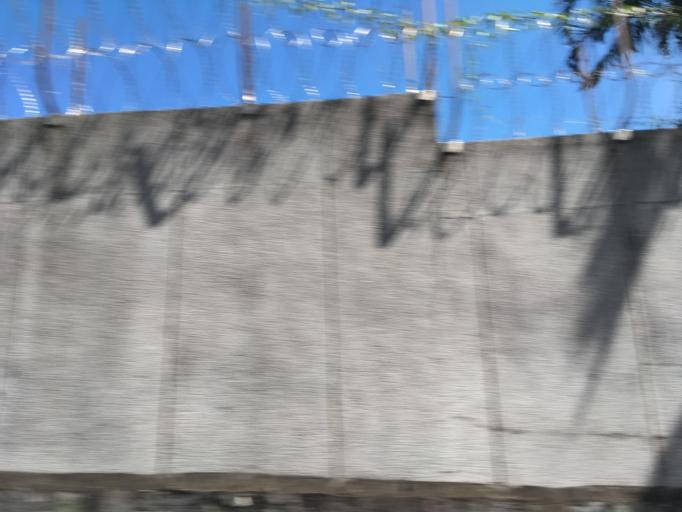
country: TW
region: Taipei
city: Taipei
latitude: 25.1474
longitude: 121.5050
